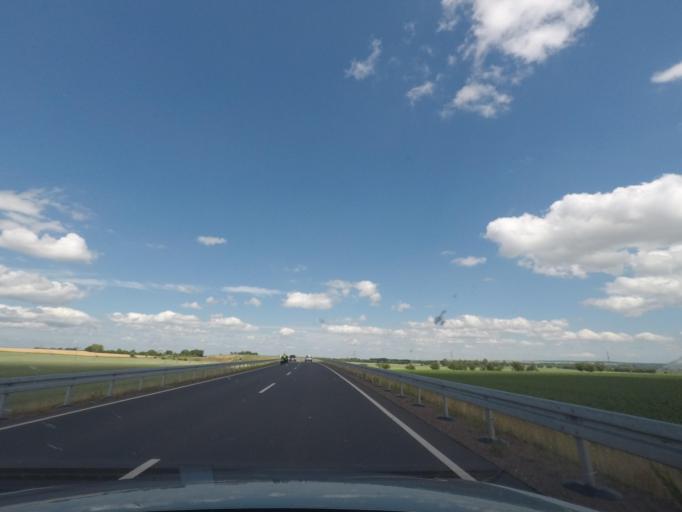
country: DE
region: Saxony-Anhalt
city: Harsleben
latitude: 51.8848
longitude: 11.1037
